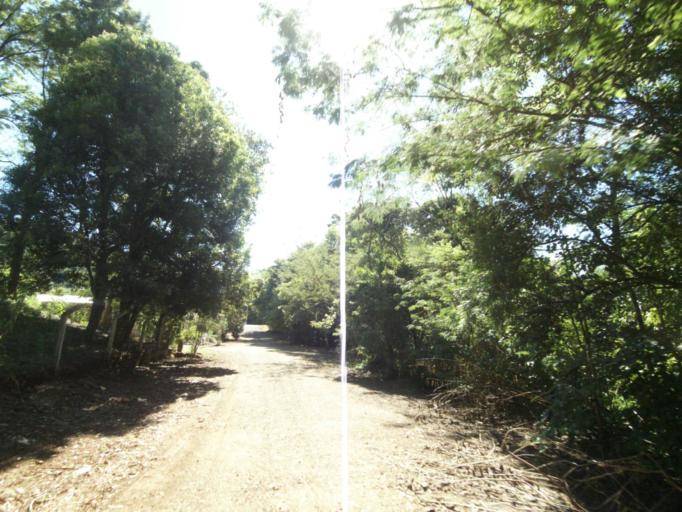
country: BR
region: Parana
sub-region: Ampere
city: Ampere
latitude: -26.1684
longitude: -53.3627
